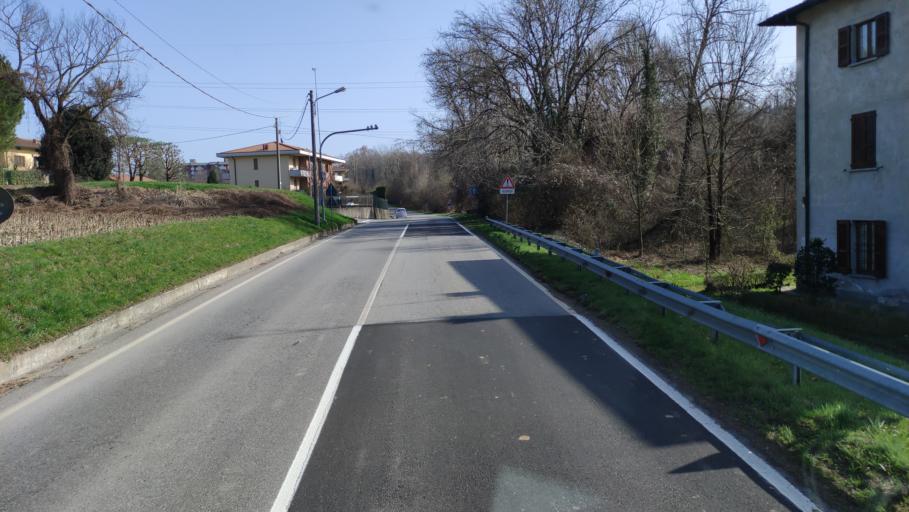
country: IT
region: Lombardy
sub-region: Provincia di Monza e Brianza
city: Capriano
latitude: 45.7333
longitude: 9.2548
